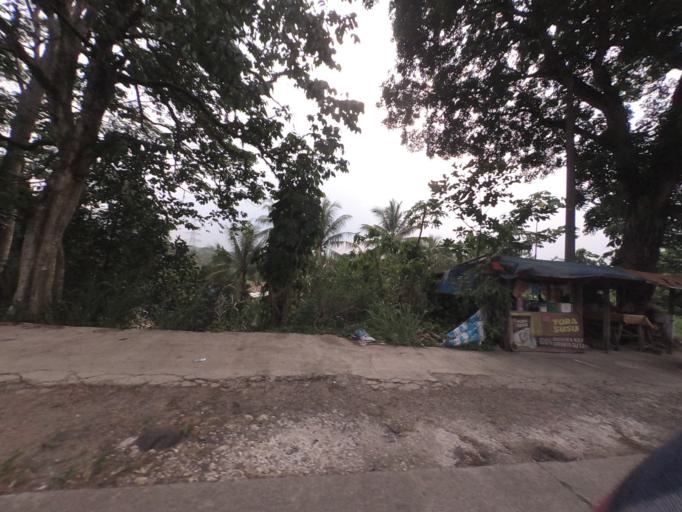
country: ID
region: West Java
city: Sidoger Lebak
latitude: -6.5602
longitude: 106.5753
